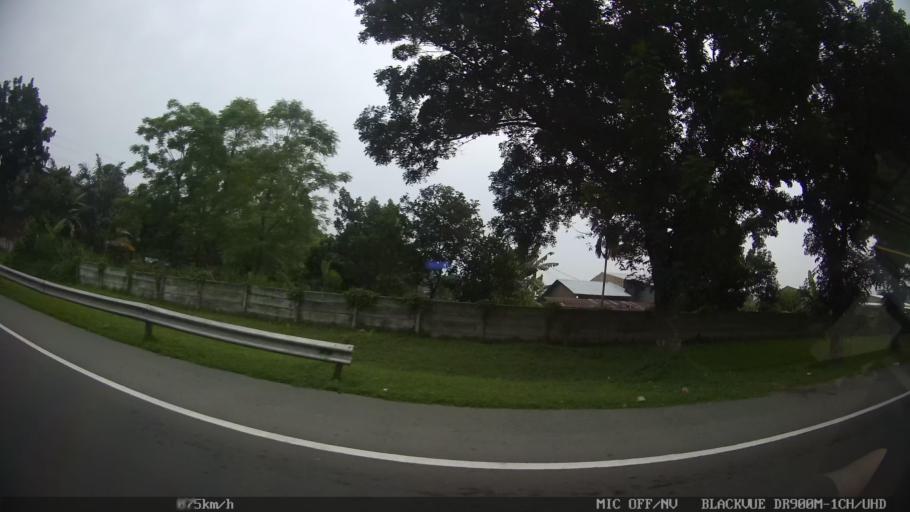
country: ID
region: North Sumatra
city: Deli Tua
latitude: 3.5535
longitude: 98.7253
